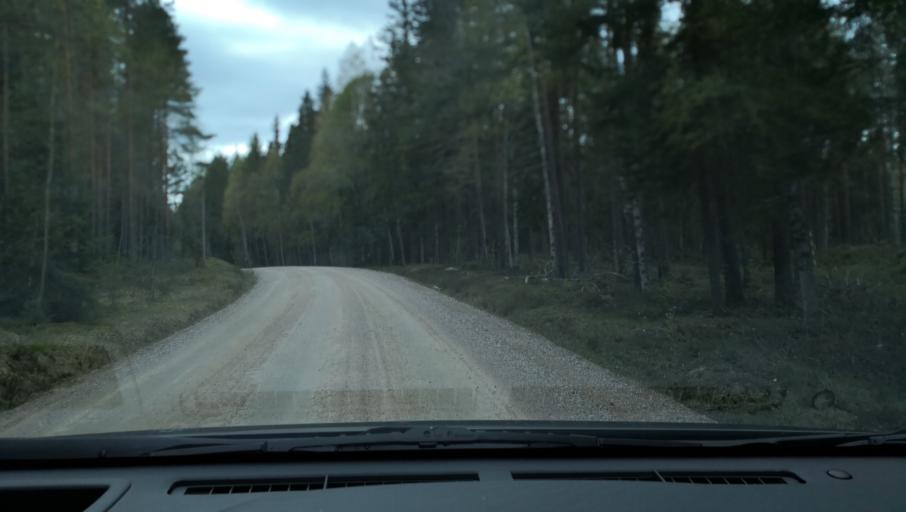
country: SE
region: Vaestmanland
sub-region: Norbergs Kommun
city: Norberg
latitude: 60.0913
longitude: 15.8628
